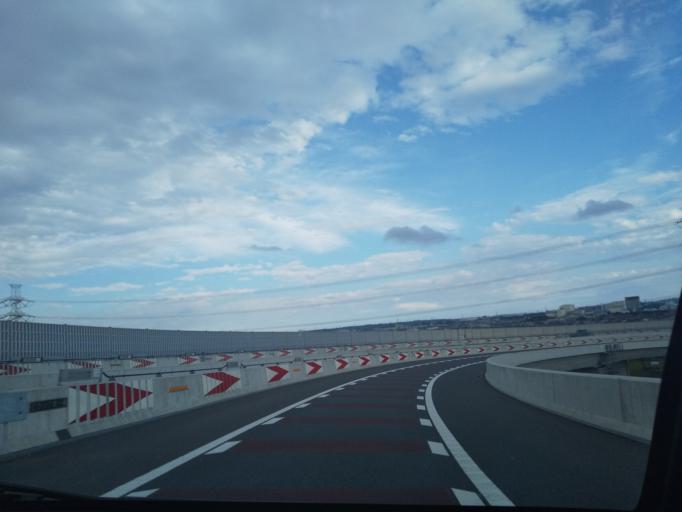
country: JP
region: Kanagawa
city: Atsugi
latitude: 35.4097
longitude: 139.3748
